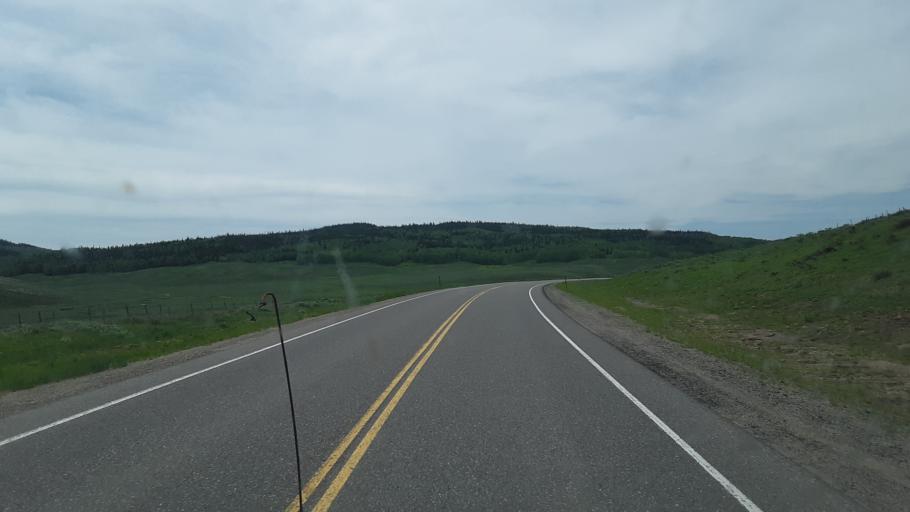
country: US
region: Colorado
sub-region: Routt County
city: Steamboat Springs
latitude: 40.4031
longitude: -106.5446
